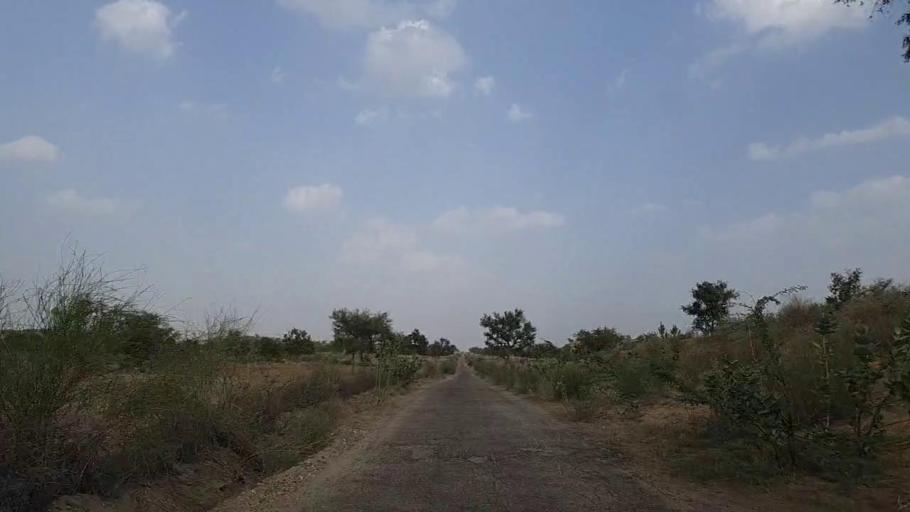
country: PK
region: Sindh
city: Islamkot
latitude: 24.7681
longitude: 70.1598
